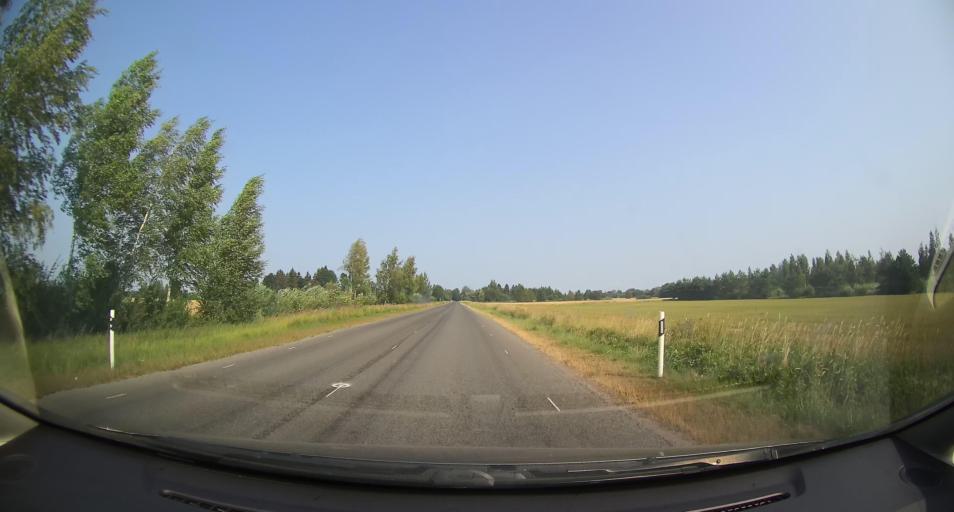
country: EE
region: Paernumaa
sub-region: Audru vald
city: Audru
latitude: 58.4569
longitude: 24.3172
